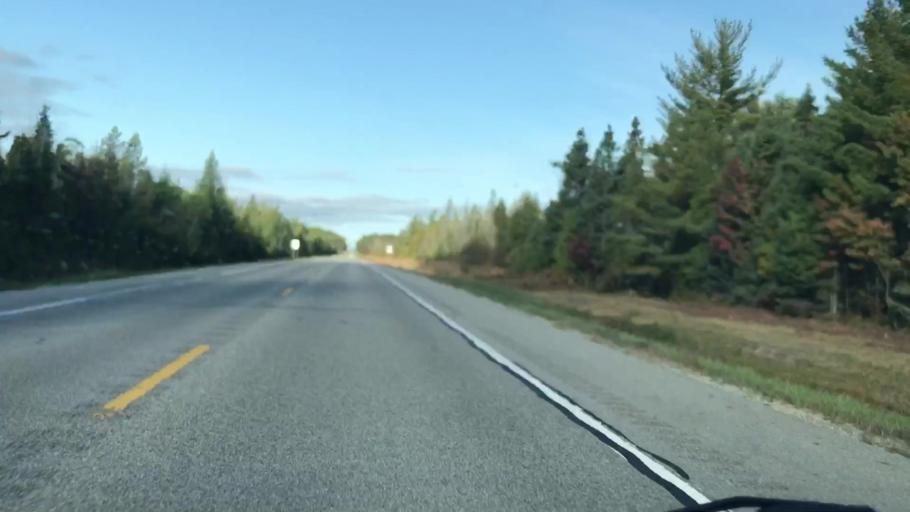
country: US
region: Michigan
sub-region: Luce County
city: Newberry
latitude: 46.3035
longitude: -85.3346
